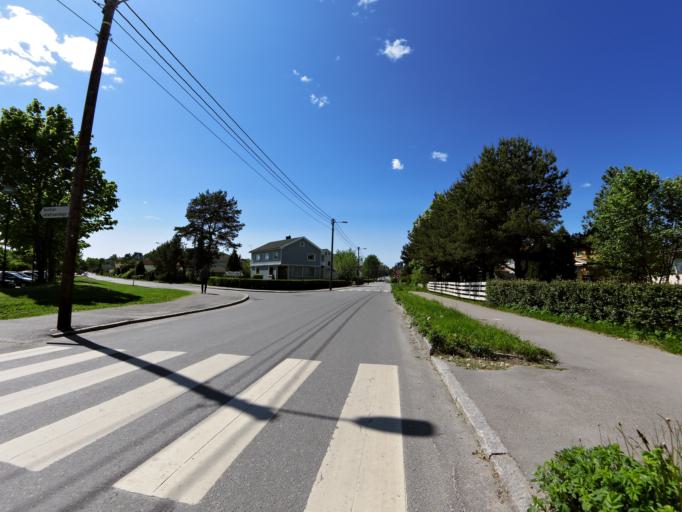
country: NO
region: Ostfold
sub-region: Fredrikstad
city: Fredrikstad
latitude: 59.2327
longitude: 10.9733
